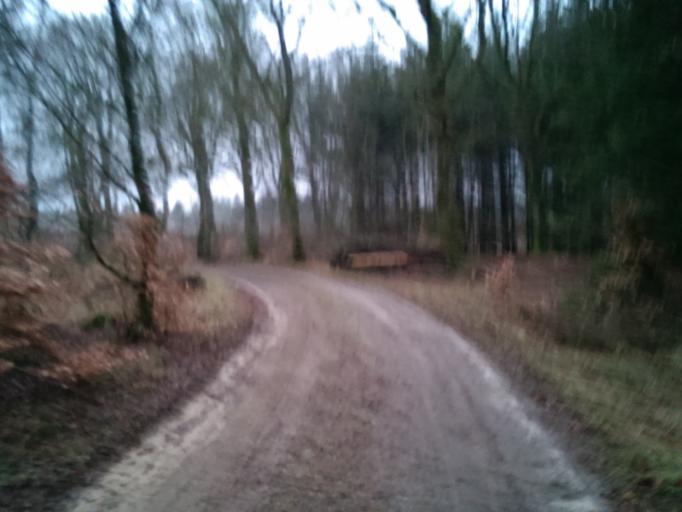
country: DK
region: North Denmark
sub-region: Mariagerfjord Kommune
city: Arden
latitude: 56.7911
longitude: 9.7564
